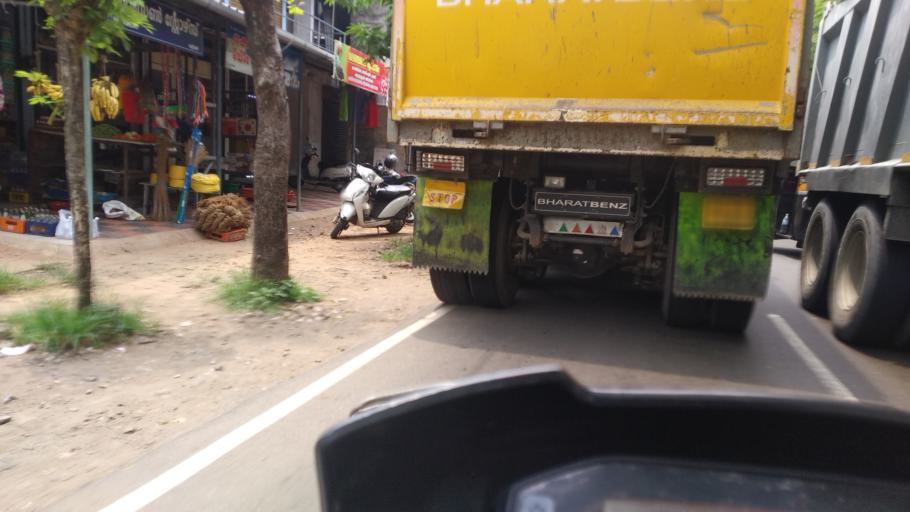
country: IN
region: Kerala
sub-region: Ernakulam
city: Aluva
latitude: 10.1565
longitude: 76.3049
